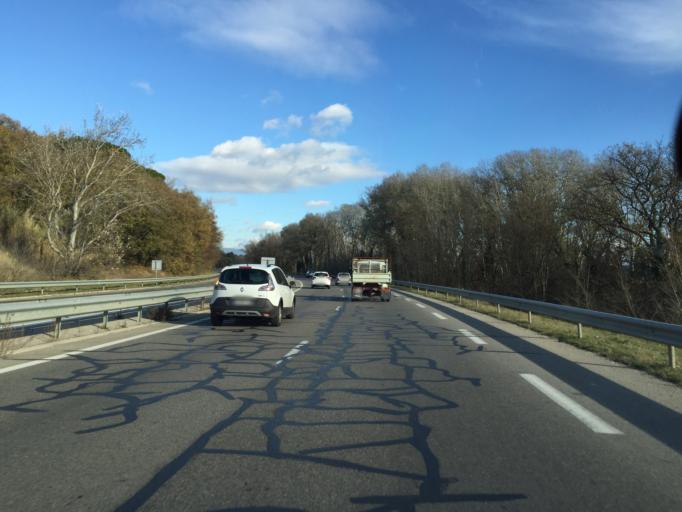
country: FR
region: Provence-Alpes-Cote d'Azur
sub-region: Departement du Vaucluse
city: Goult
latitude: 43.8545
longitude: 5.2532
